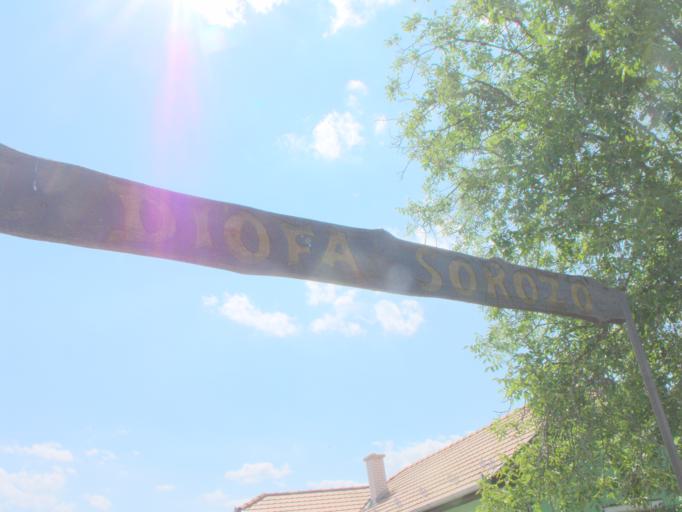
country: HU
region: Pest
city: Inarcs
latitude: 47.2679
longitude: 19.3186
